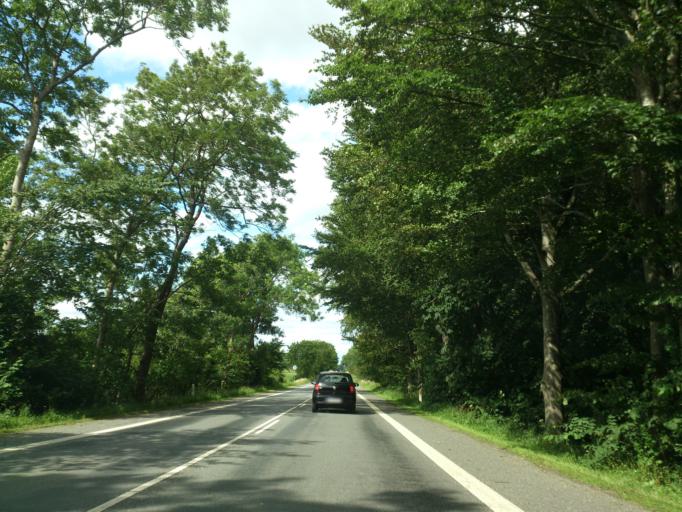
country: DK
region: South Denmark
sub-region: Aabenraa Kommune
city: Krusa
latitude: 54.9118
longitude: 9.4422
